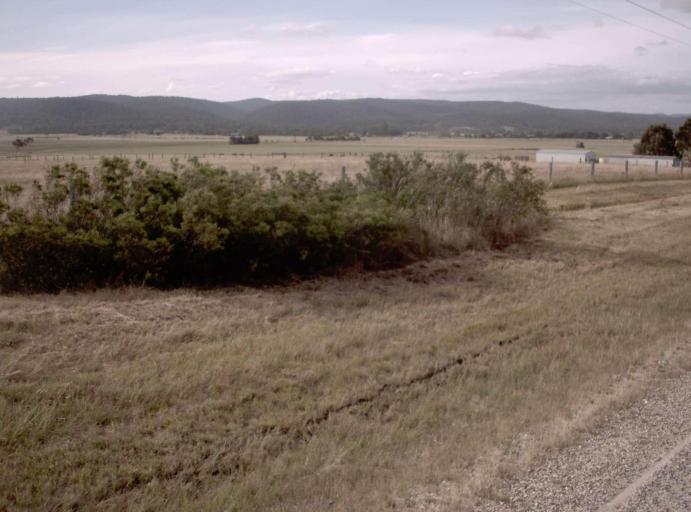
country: AU
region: Victoria
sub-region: Wellington
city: Heyfield
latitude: -38.0250
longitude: 146.6690
